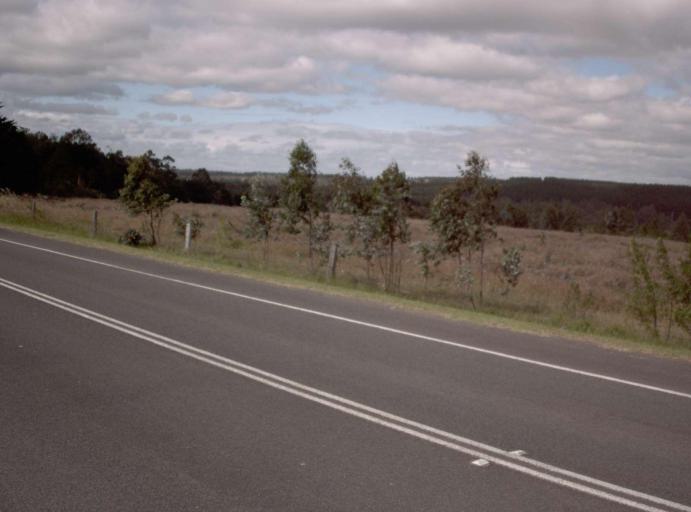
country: AU
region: Victoria
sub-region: Latrobe
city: Morwell
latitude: -38.1901
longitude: 146.4510
